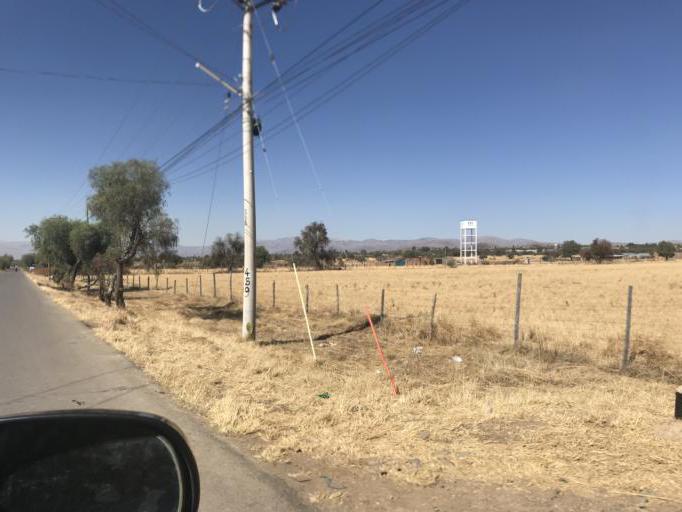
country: BO
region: Cochabamba
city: Tarata
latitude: -17.6105
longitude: -66.0127
